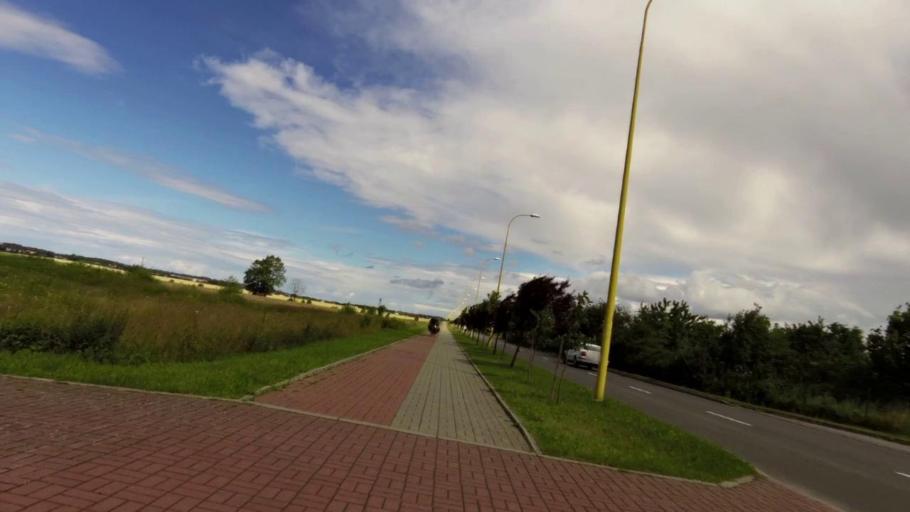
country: PL
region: West Pomeranian Voivodeship
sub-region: Powiat slawienski
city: Darlowo
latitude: 54.4300
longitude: 16.4136
